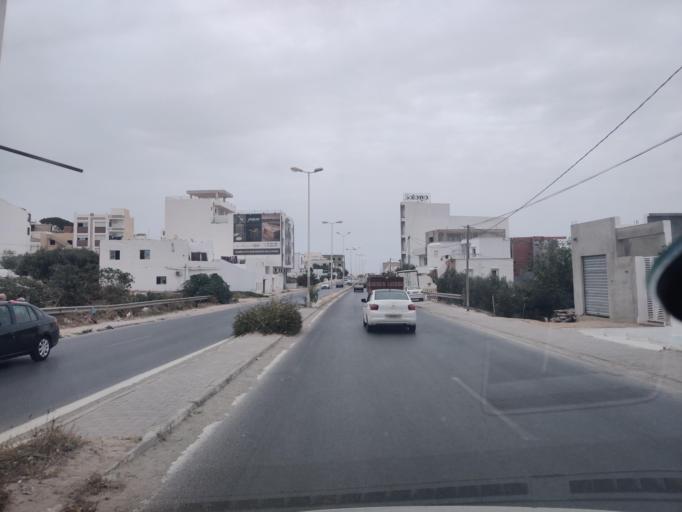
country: TN
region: Nabul
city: Al Hammamat
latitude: 36.4089
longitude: 10.6265
